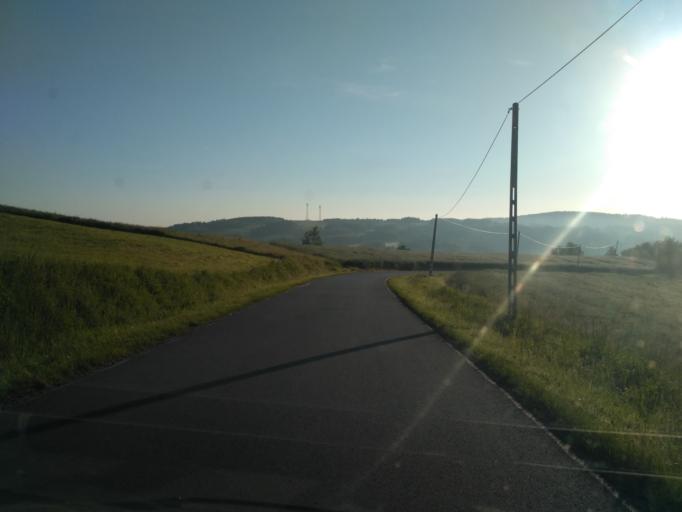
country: PL
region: Subcarpathian Voivodeship
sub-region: Powiat strzyzowski
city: Polomia
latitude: 49.8968
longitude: 21.8670
